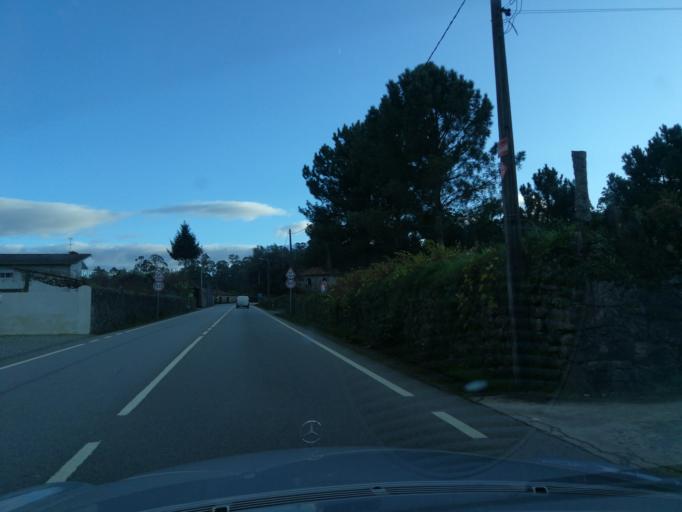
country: PT
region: Braga
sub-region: Esposende
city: Marinhas
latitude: 41.5919
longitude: -8.7369
